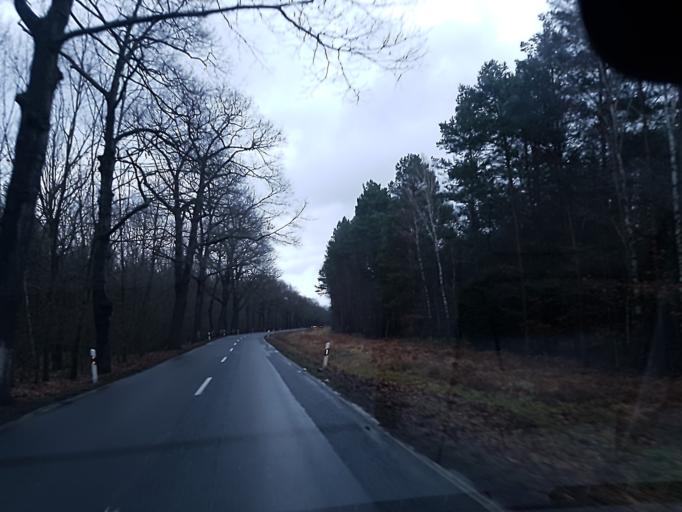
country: DE
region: Brandenburg
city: Hohenleipisch
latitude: 51.5259
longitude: 13.5808
